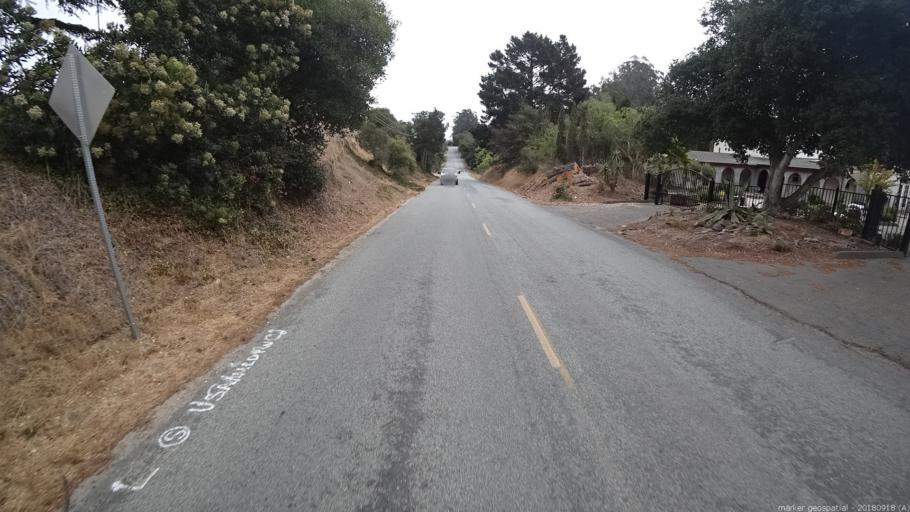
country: US
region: California
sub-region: Monterey County
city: Prunedale
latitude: 36.7770
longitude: -121.6611
